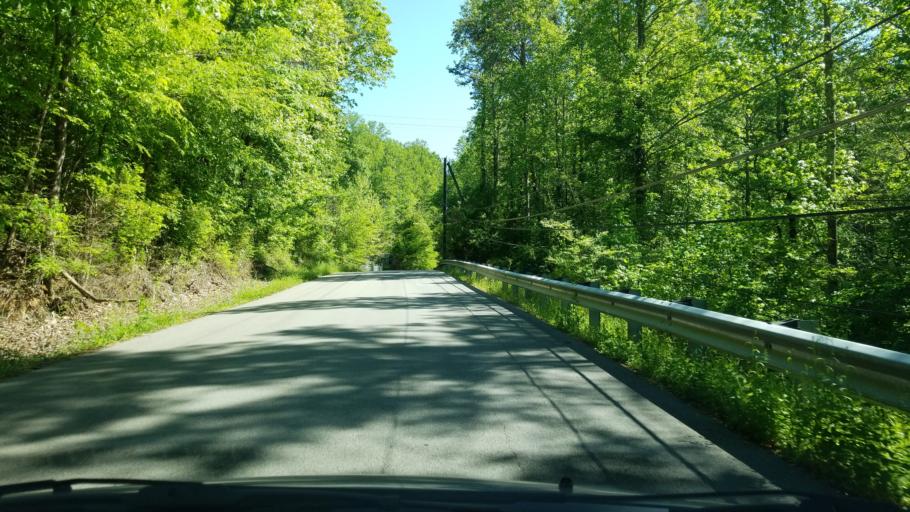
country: US
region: Tennessee
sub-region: Hamilton County
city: Walden
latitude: 35.1490
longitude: -85.2975
